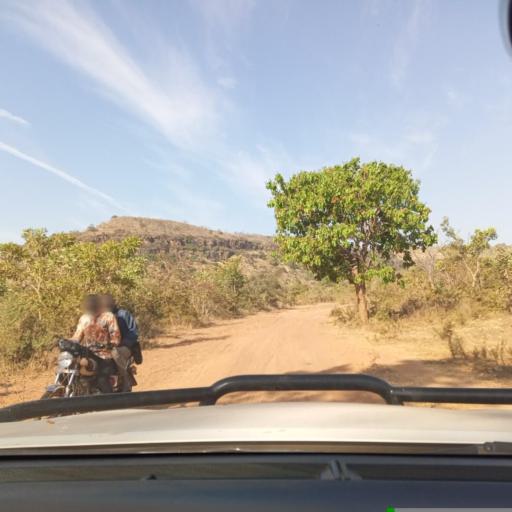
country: ML
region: Bamako
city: Bamako
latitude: 12.5570
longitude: -8.1489
